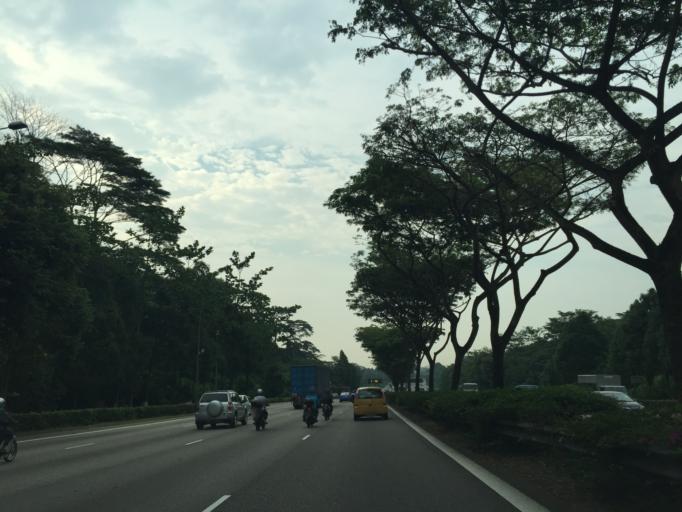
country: MY
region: Johor
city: Johor Bahru
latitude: 1.4110
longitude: 103.7715
